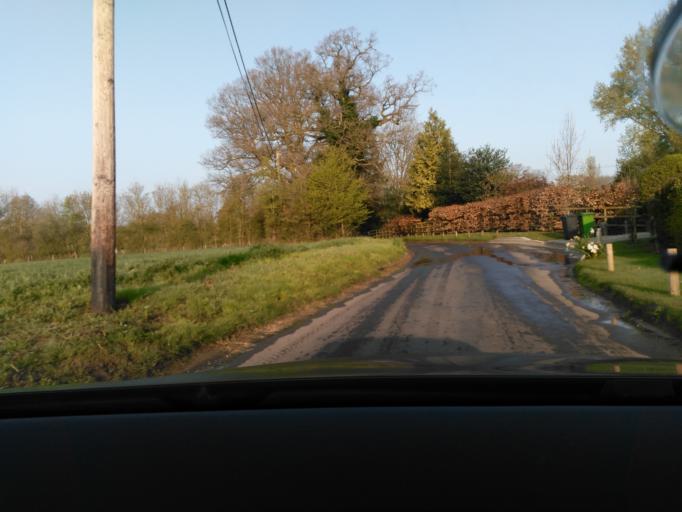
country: GB
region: England
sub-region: Hampshire
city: Tadley
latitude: 51.3468
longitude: -1.0801
